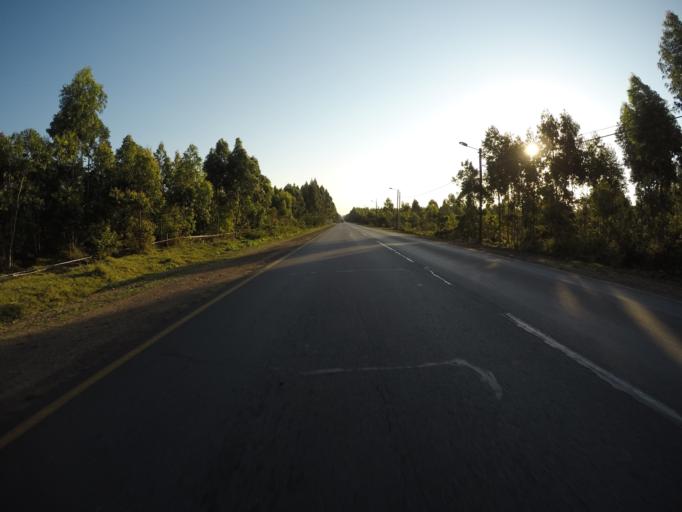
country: ZA
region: KwaZulu-Natal
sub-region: uThungulu District Municipality
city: KwaMbonambi
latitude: -28.6831
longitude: 32.1891
